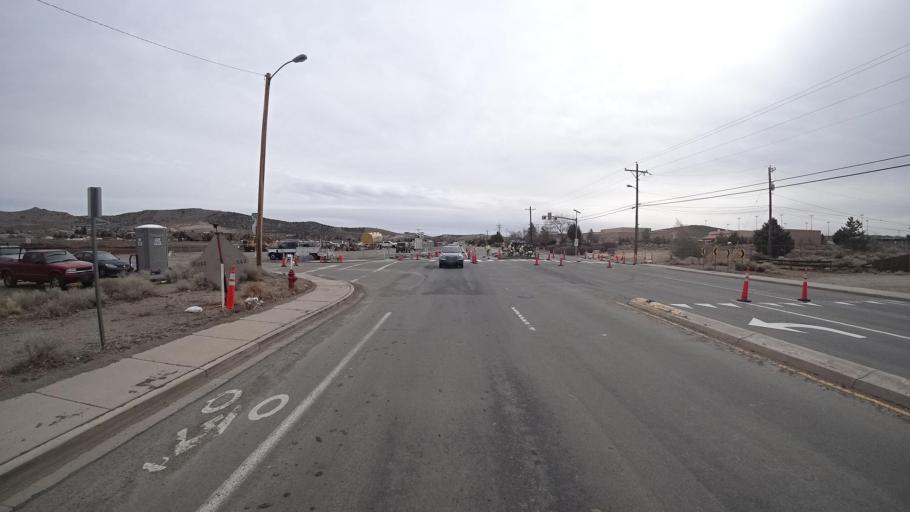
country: US
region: Nevada
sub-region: Washoe County
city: Golden Valley
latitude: 39.6081
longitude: -119.8269
